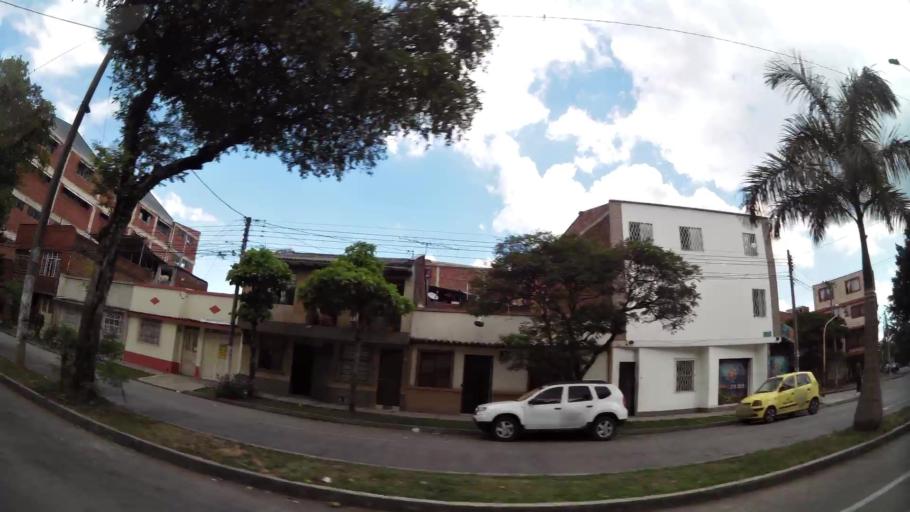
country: CO
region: Valle del Cauca
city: Cali
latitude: 3.4362
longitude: -76.5308
